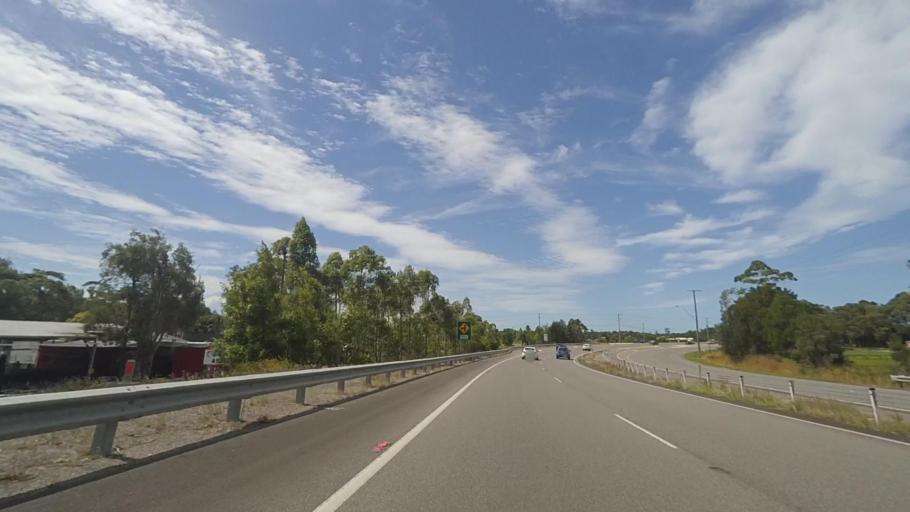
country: AU
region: New South Wales
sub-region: Port Stephens Shire
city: Anna Bay
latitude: -32.7681
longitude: 152.0122
